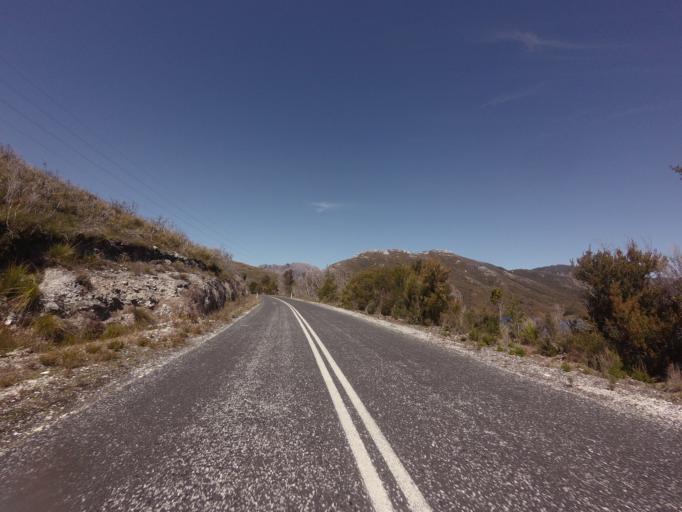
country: AU
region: Tasmania
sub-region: Huon Valley
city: Geeveston
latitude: -42.8471
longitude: 146.1705
